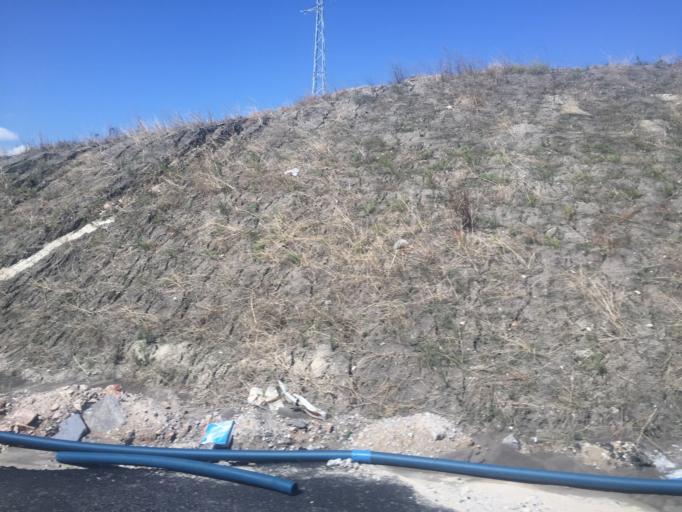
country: TR
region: Balikesir
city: Susurluk
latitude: 39.9626
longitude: 28.1646
